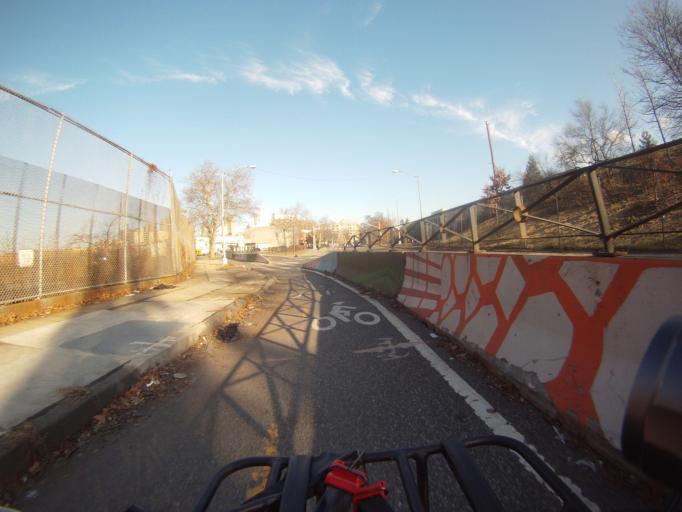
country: US
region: New York
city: New York City
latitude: 40.6997
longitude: -73.9624
